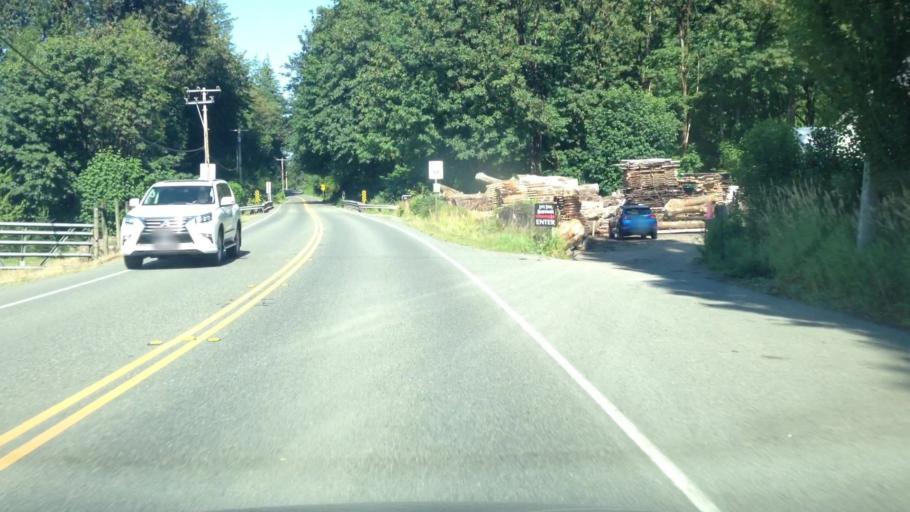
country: US
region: Washington
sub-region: King County
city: Duvall
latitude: 47.7431
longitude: -121.9426
